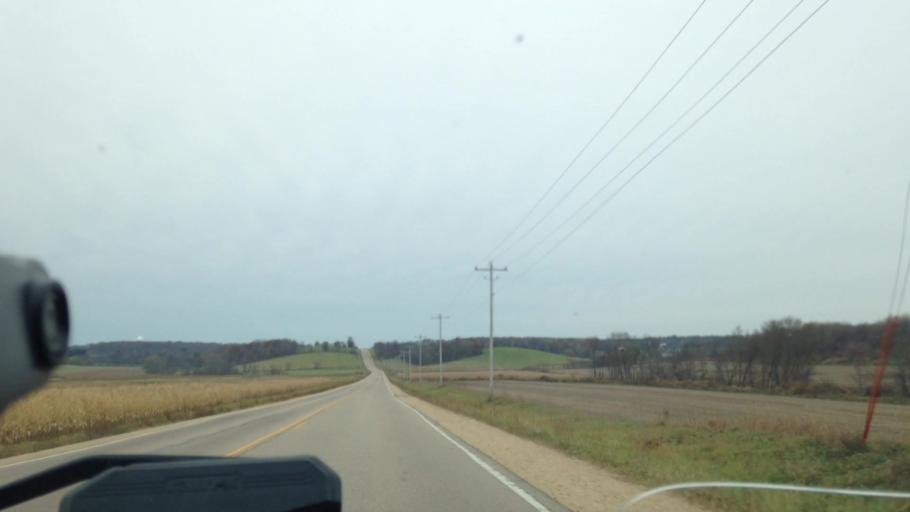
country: US
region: Wisconsin
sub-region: Dodge County
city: Mayville
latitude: 43.4707
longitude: -88.4993
